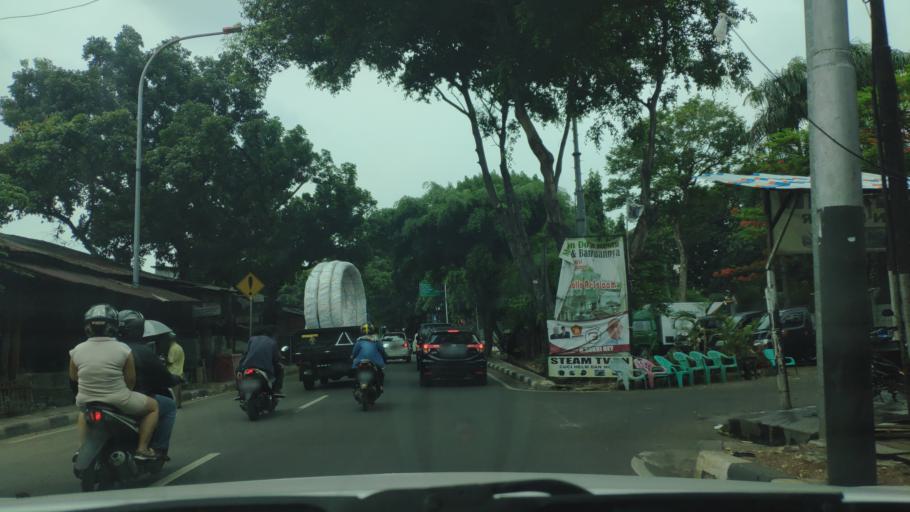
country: ID
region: Jakarta Raya
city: Jakarta
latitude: -6.1894
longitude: 106.7830
